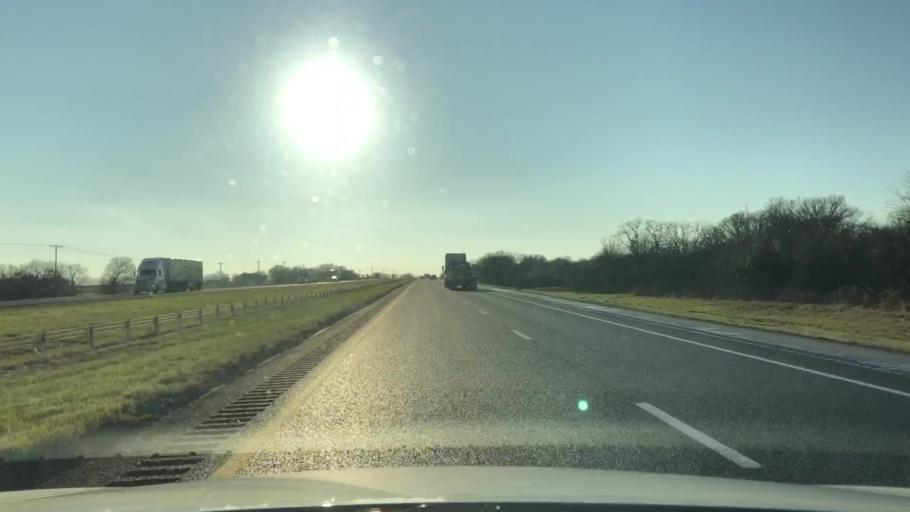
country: US
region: Texas
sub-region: Gonzales County
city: Waelder
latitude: 29.6751
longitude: -97.2853
